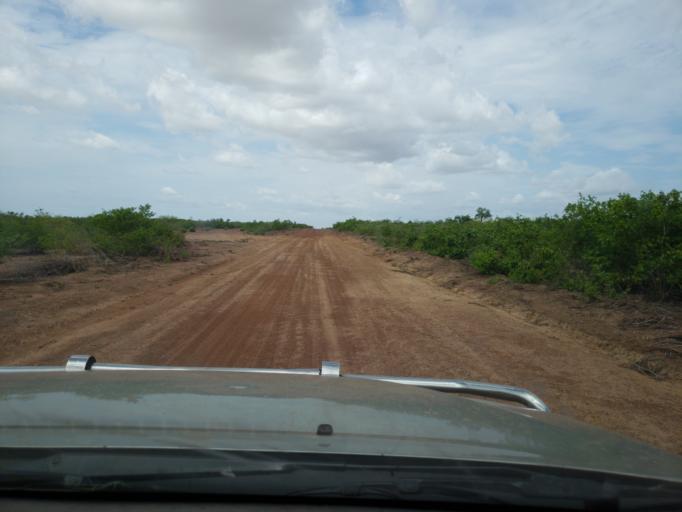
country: ML
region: Segou
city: Bla
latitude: 12.7083
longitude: -5.6982
